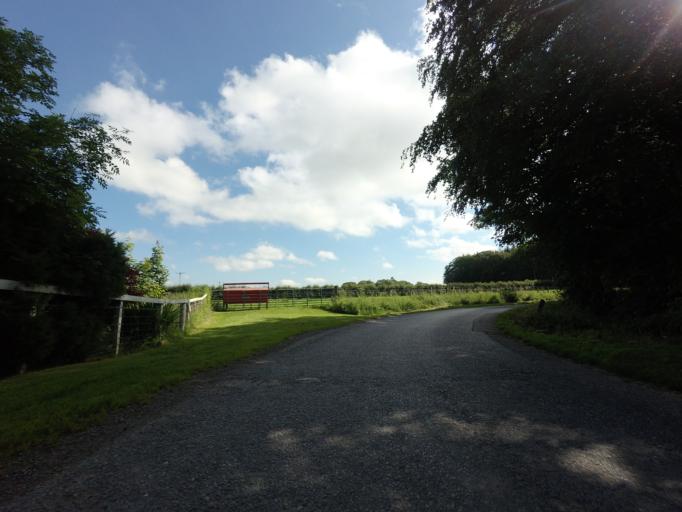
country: GB
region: Scotland
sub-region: Aberdeenshire
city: Turriff
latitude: 57.5887
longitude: -2.5040
